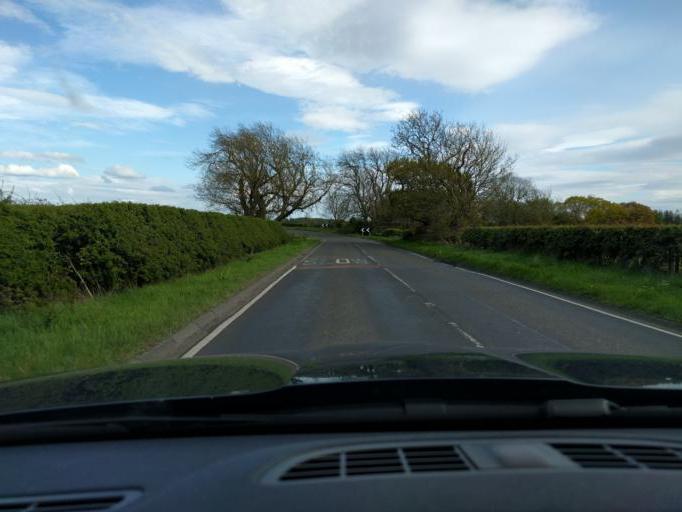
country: GB
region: England
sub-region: Northumberland
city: Stannington
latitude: 55.1252
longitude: -1.6385
